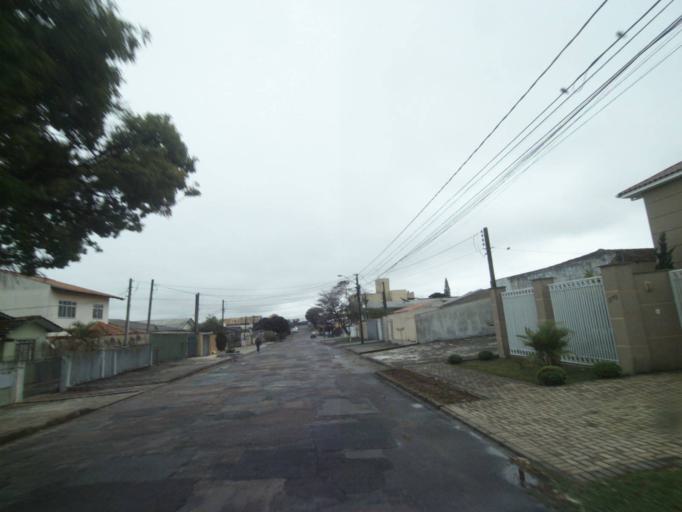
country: BR
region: Parana
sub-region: Curitiba
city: Curitiba
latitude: -25.5111
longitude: -49.2997
